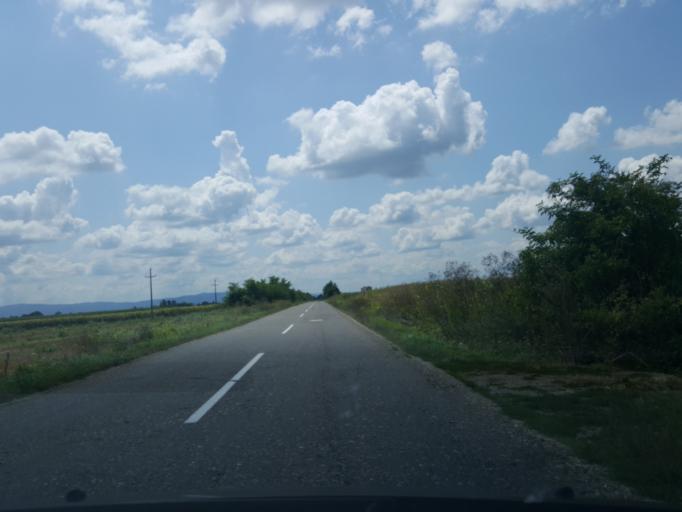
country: RS
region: Central Serbia
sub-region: Macvanski Okrug
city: Bogatic
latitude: 44.8079
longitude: 19.4751
